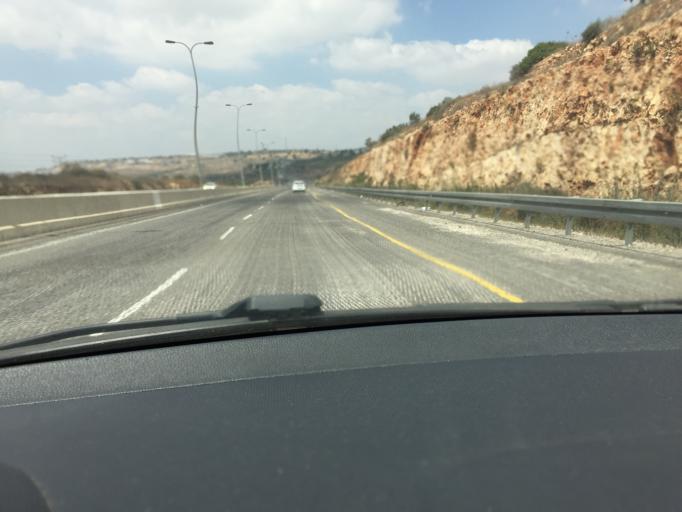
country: PS
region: West Bank
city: Haris
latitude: 32.1093
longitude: 35.1489
